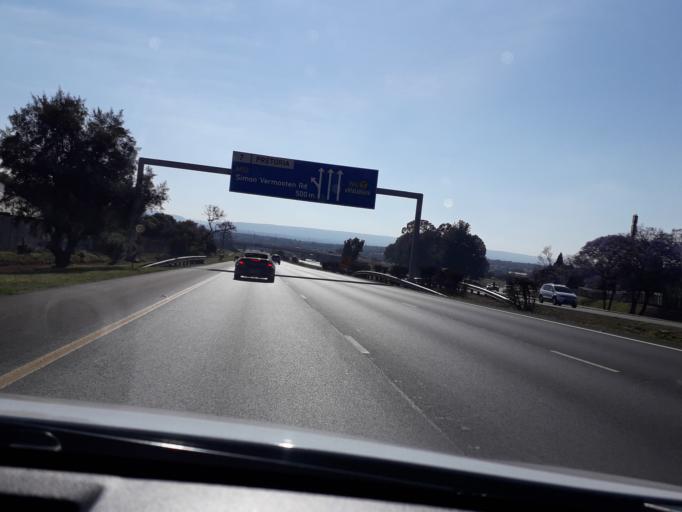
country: ZA
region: Gauteng
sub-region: City of Tshwane Metropolitan Municipality
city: Pretoria
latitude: -25.7526
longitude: 28.3194
